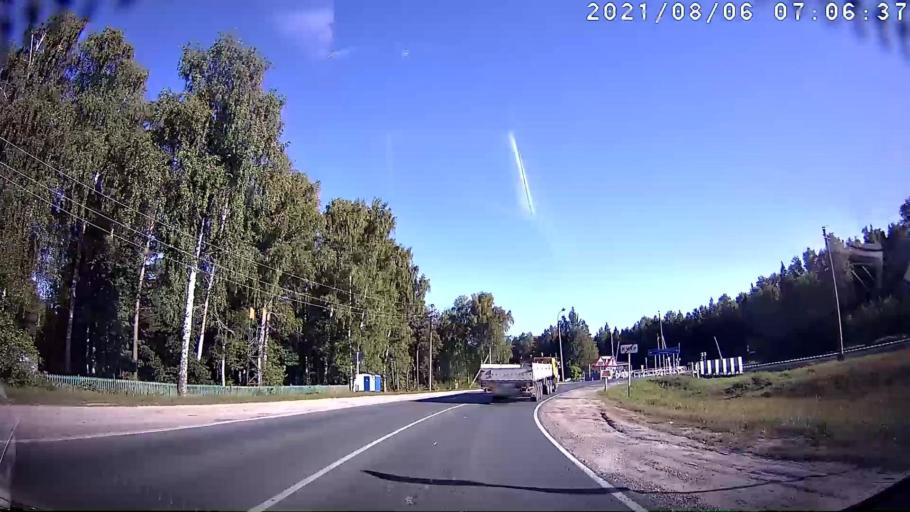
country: RU
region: Mariy-El
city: Yoshkar-Ola
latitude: 56.5599
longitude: 47.9802
